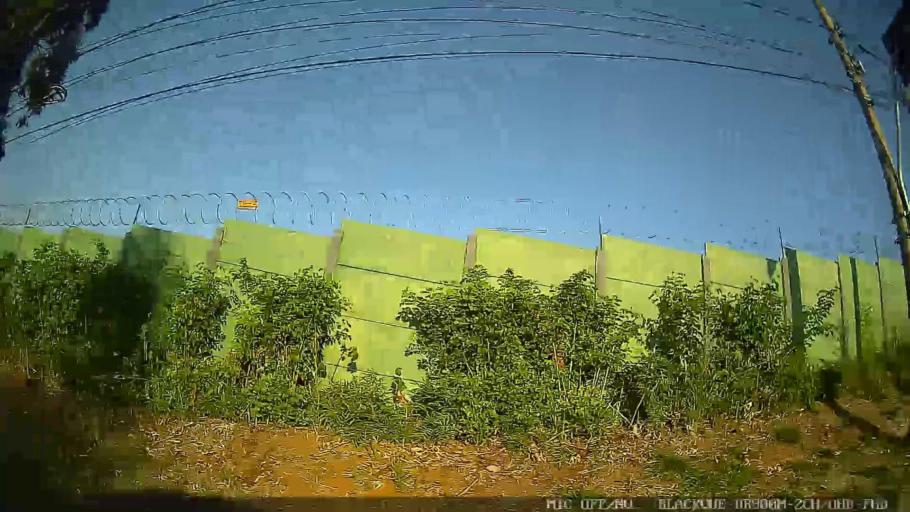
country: BR
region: Sao Paulo
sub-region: Cabreuva
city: Cabreuva
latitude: -23.2680
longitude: -47.0574
